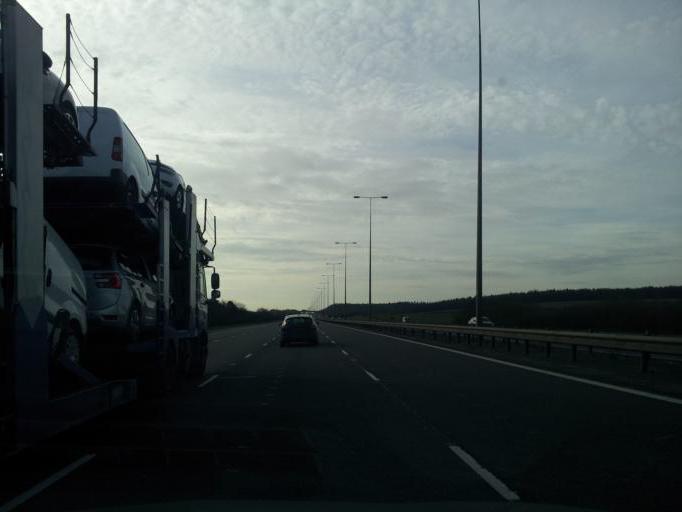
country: GB
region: England
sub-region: Cambridgeshire
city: Sawtry
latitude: 52.4169
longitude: -0.2672
